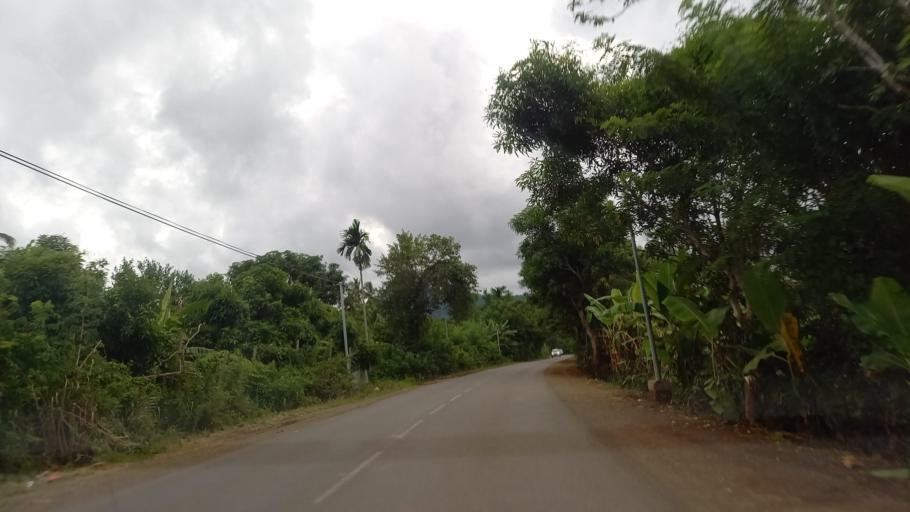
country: YT
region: Chirongui
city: Chirongui
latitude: -12.9235
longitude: 45.1567
